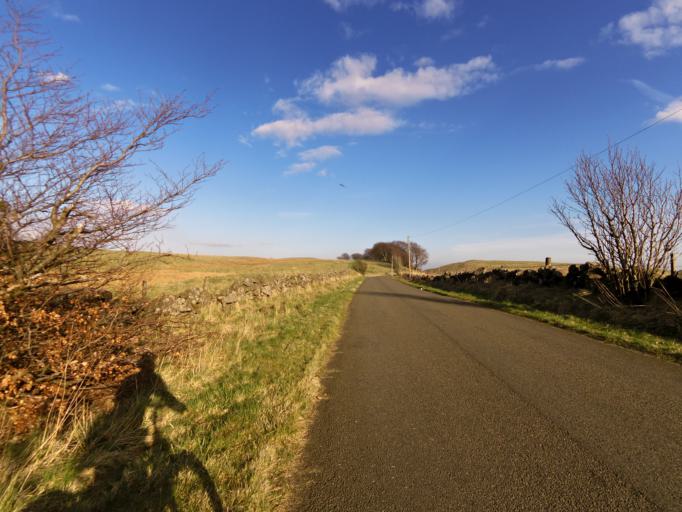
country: GB
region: Scotland
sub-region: Fife
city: Falkland
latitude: 56.2356
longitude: -3.2418
